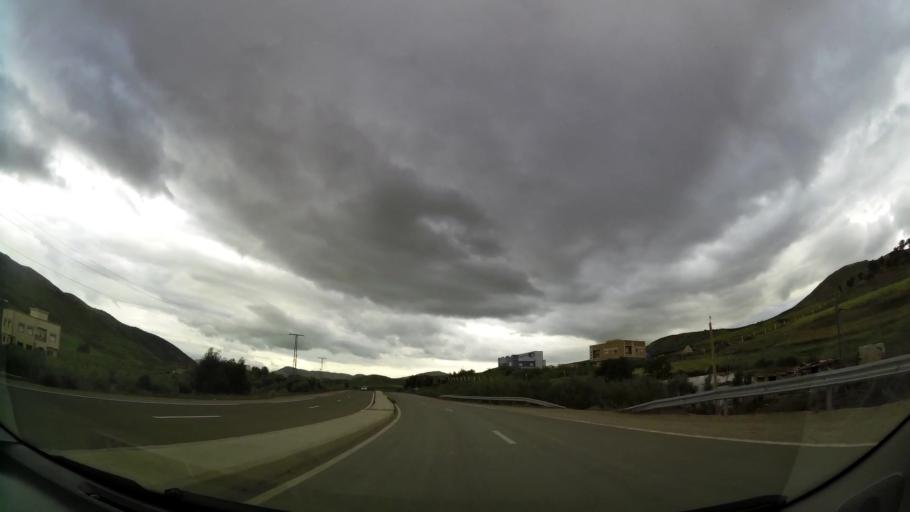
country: MA
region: Taza-Al Hoceima-Taounate
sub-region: Taza
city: Taza
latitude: 34.3398
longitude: -3.9364
